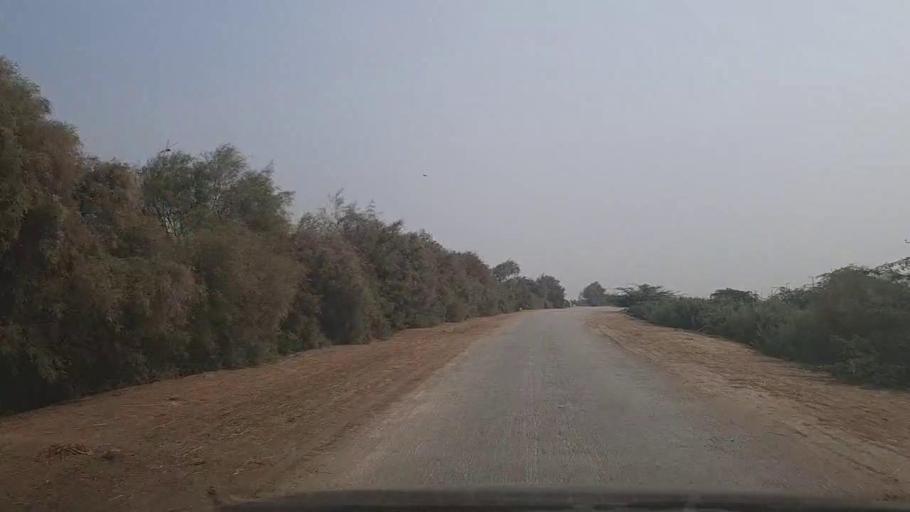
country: PK
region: Sindh
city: Mirpur Sakro
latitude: 24.4784
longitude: 67.6591
